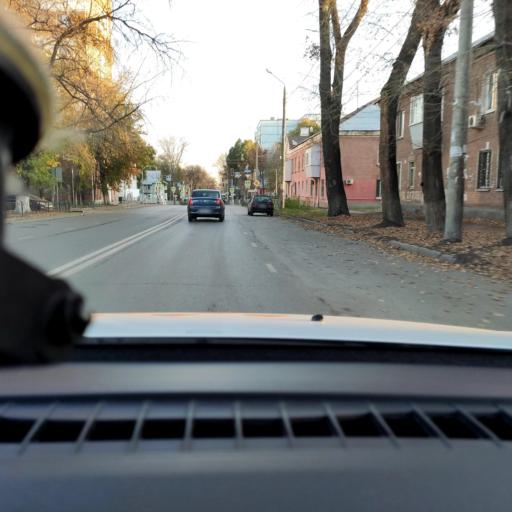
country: RU
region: Samara
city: Samara
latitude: 53.2297
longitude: 50.2531
